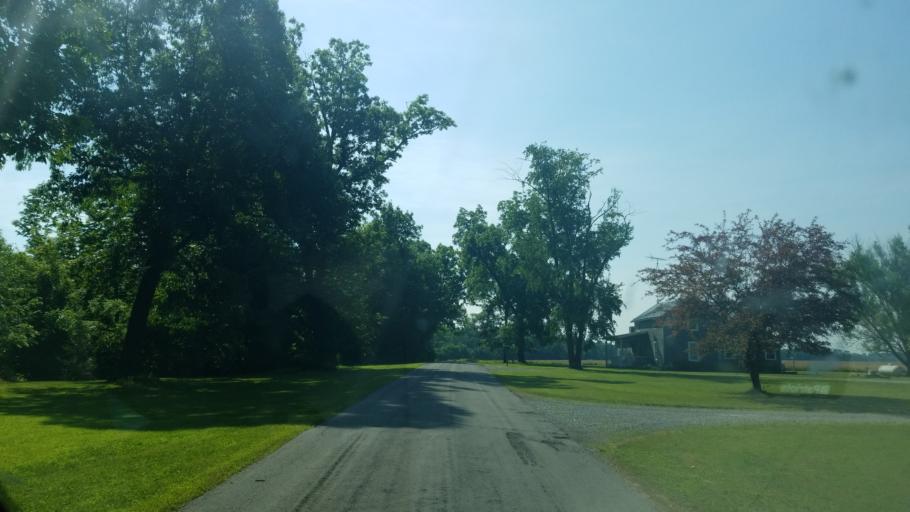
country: US
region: Ohio
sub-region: Wyandot County
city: Upper Sandusky
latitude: 40.9049
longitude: -83.2540
